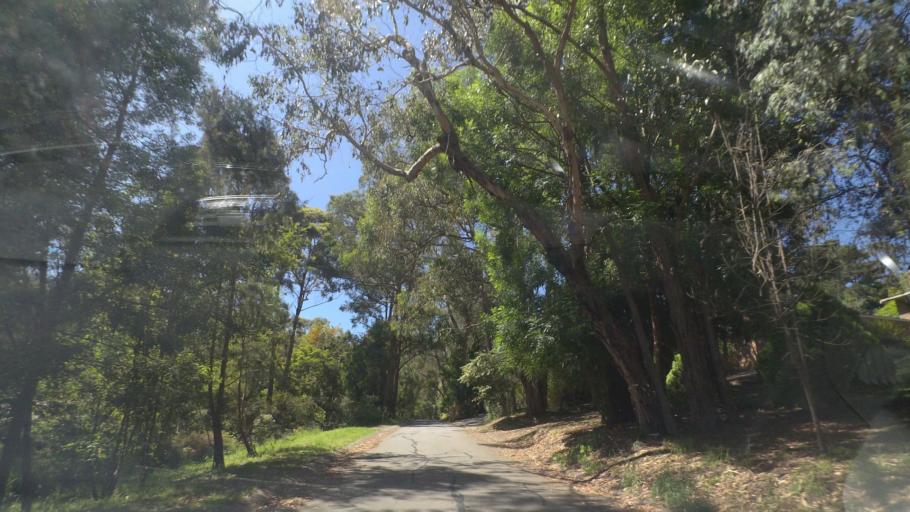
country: AU
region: Victoria
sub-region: Yarra Ranges
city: Mount Evelyn
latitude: -37.7986
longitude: 145.3760
